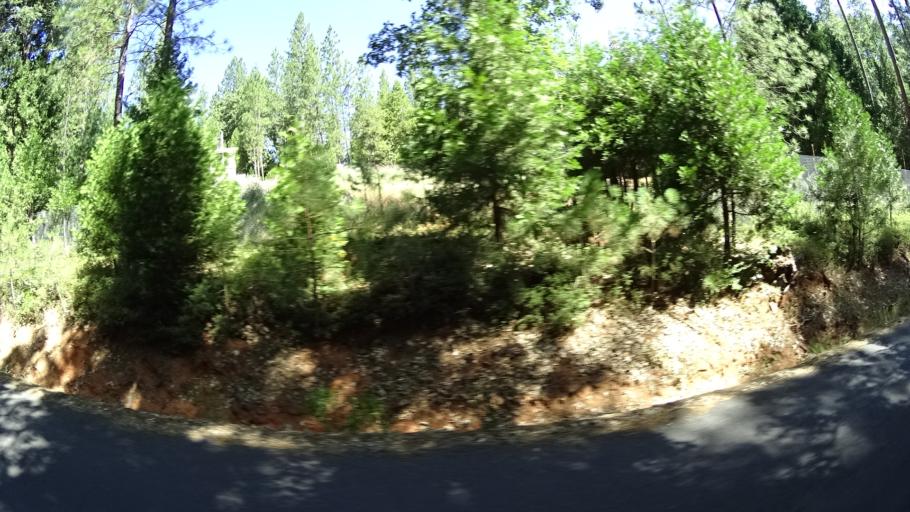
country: US
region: California
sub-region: Amador County
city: Pioneer
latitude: 38.4012
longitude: -120.5034
